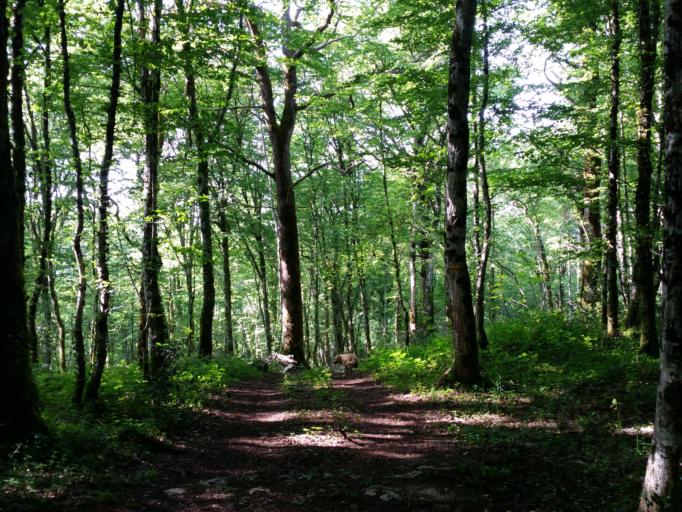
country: FR
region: Franche-Comte
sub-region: Departement du Doubs
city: Quingey
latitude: 47.0500
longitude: 5.9821
